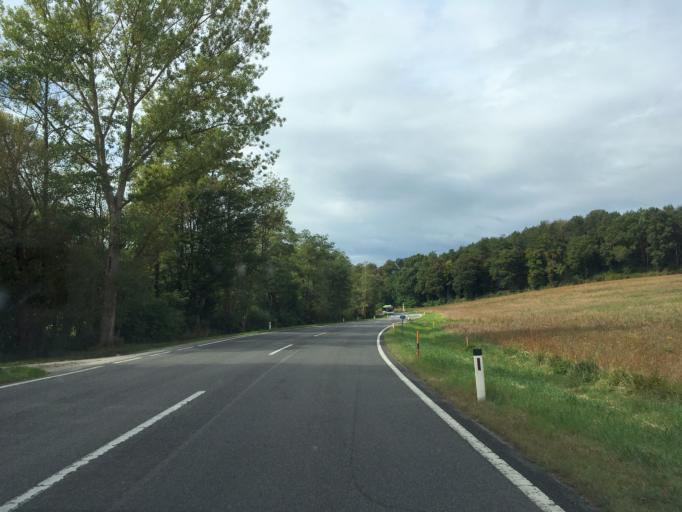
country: AT
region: Lower Austria
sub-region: Politischer Bezirk Modling
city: Gaaden
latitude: 48.0534
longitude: 16.1909
